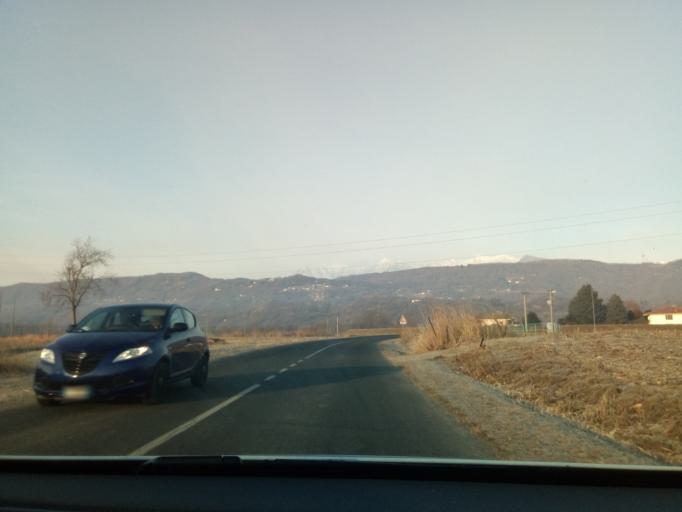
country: IT
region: Piedmont
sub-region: Provincia di Torino
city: Salerano Canavese
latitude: 45.4633
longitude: 7.8450
